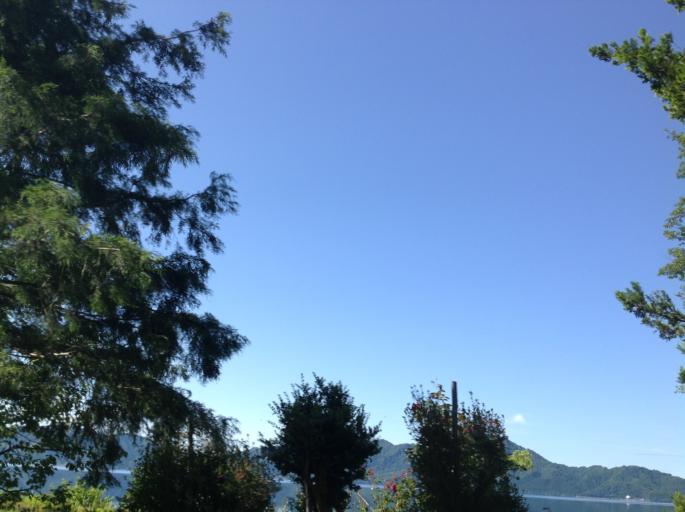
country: JP
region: Akita
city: Kakunodatemachi
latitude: 39.7485
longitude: 140.6691
